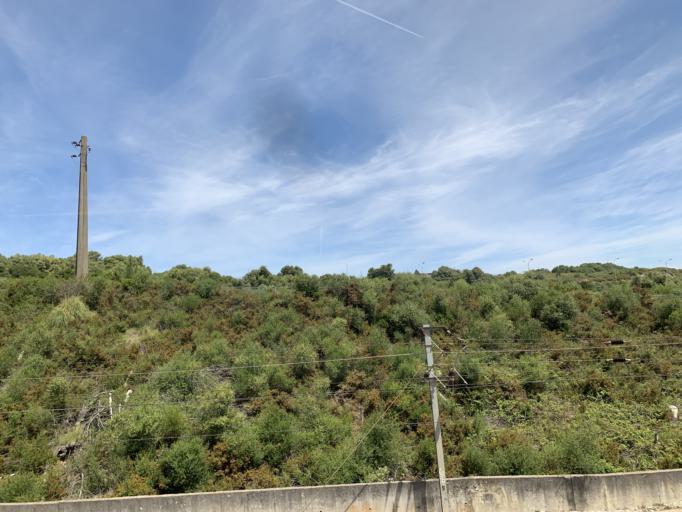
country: PT
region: Lisbon
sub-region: Sintra
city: Sintra
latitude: 38.8015
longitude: -9.3614
